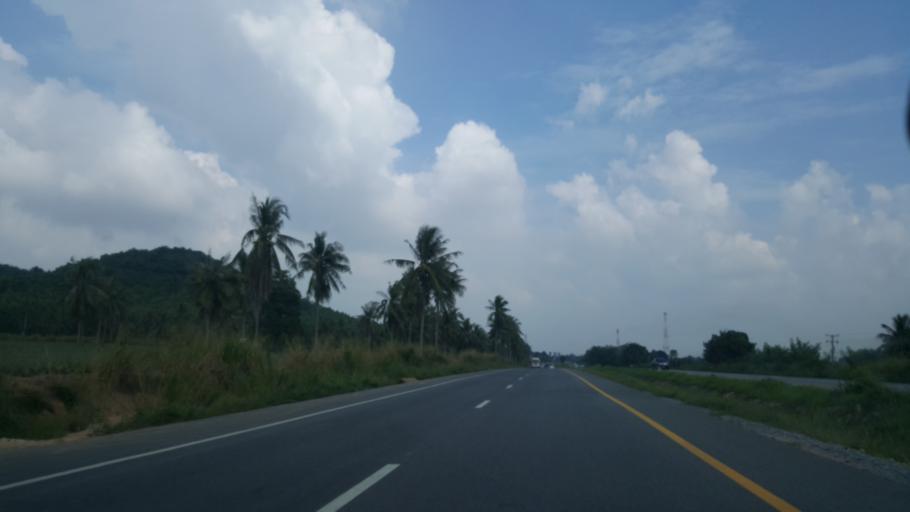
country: TH
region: Rayong
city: Ban Chang
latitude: 12.8003
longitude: 100.9920
